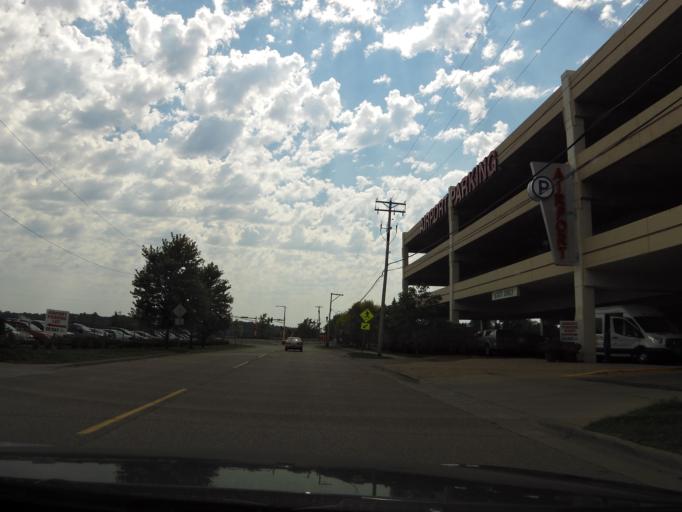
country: US
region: Minnesota
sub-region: Dakota County
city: Mendota Heights
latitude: 44.8976
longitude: -93.1722
